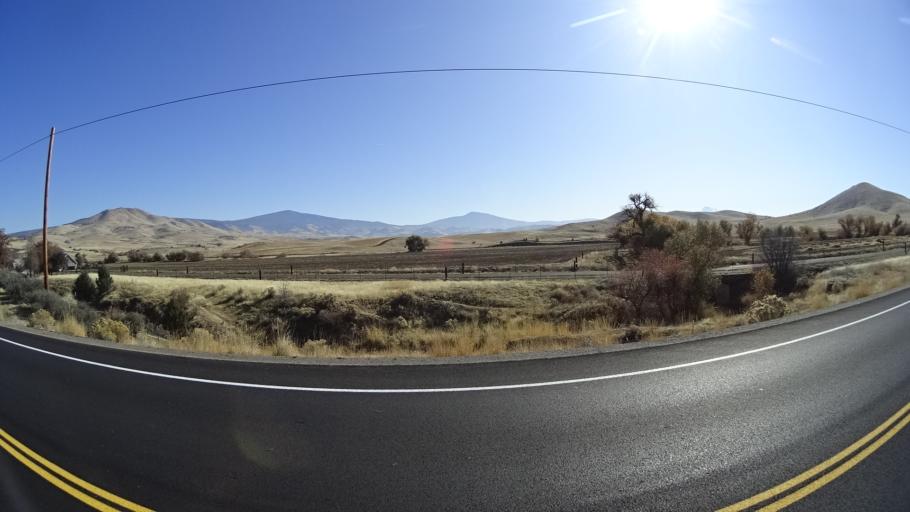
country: US
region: California
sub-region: Siskiyou County
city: Montague
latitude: 41.8441
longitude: -122.4752
